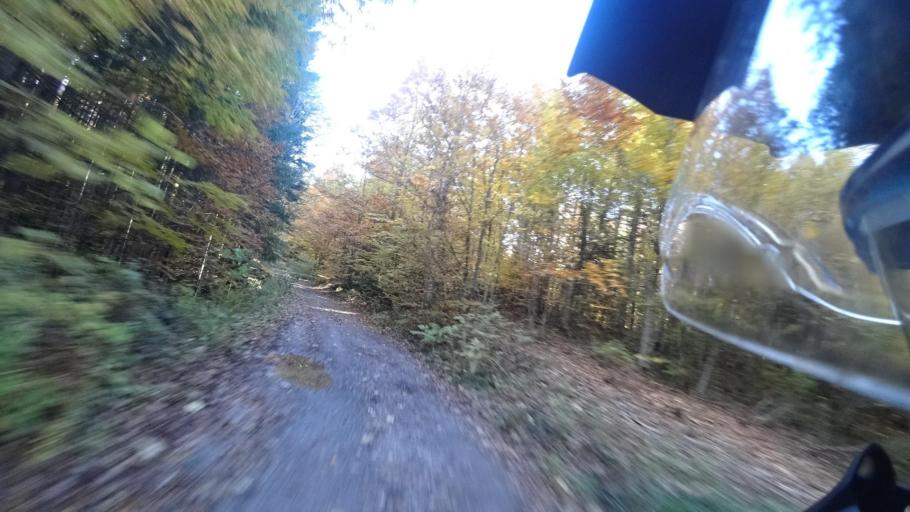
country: HR
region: Karlovacka
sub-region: Grad Ogulin
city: Ogulin
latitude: 45.2016
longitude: 15.1113
